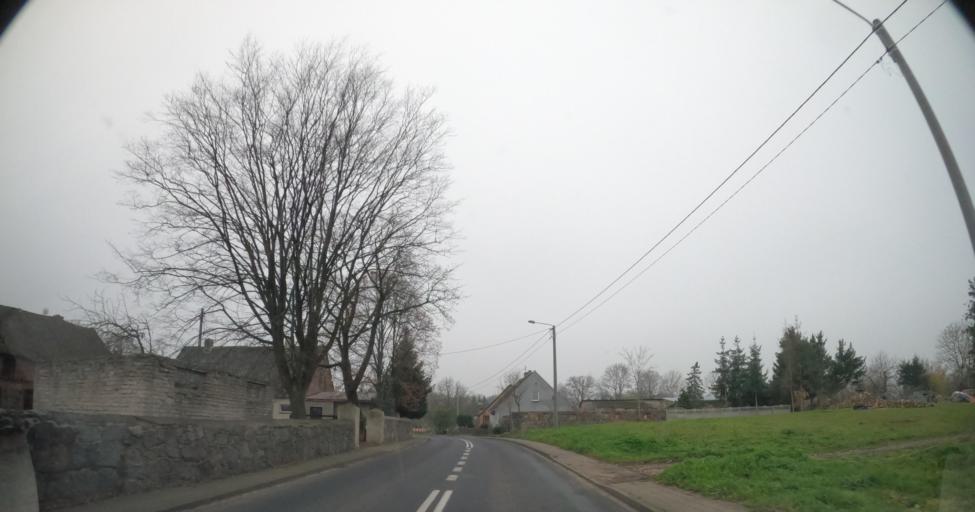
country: PL
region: West Pomeranian Voivodeship
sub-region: Powiat drawski
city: Drawsko Pomorskie
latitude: 53.5877
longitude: 15.7327
